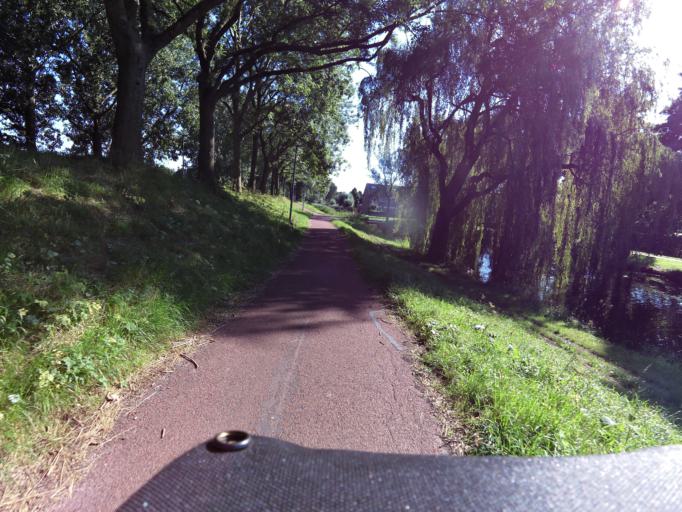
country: NL
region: South Holland
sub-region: Gemeente Dordrecht
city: Dordrecht
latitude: 51.7791
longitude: 4.6876
